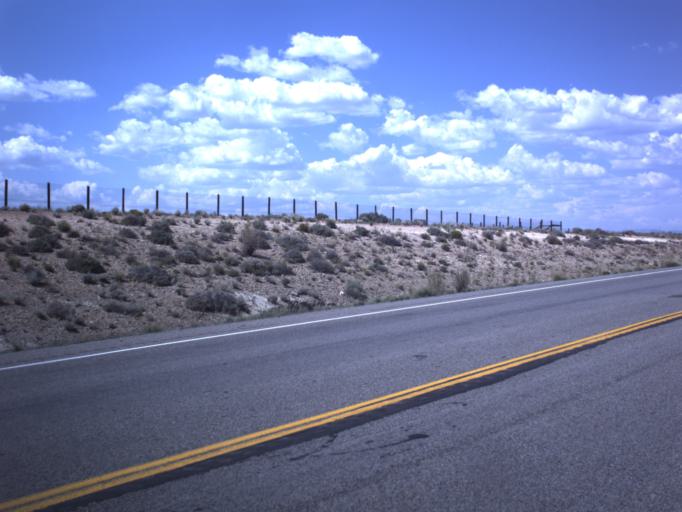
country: US
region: Utah
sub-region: Carbon County
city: Price
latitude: 39.4769
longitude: -110.8539
